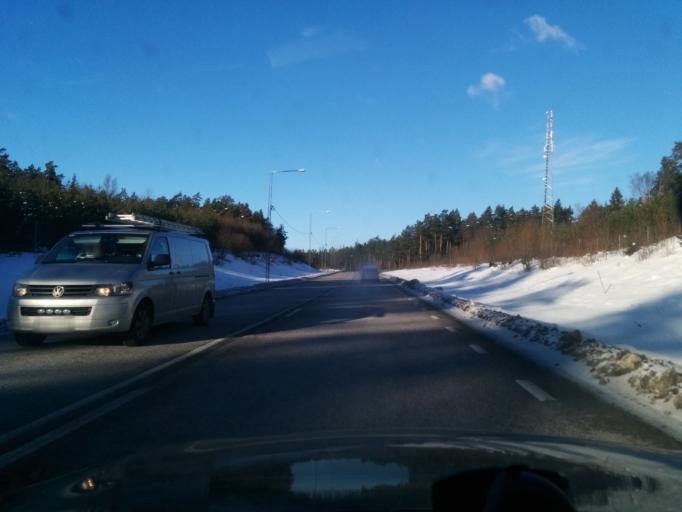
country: SE
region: Stockholm
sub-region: Vallentuna Kommun
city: Vallentuna
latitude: 59.4920
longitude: 18.1086
